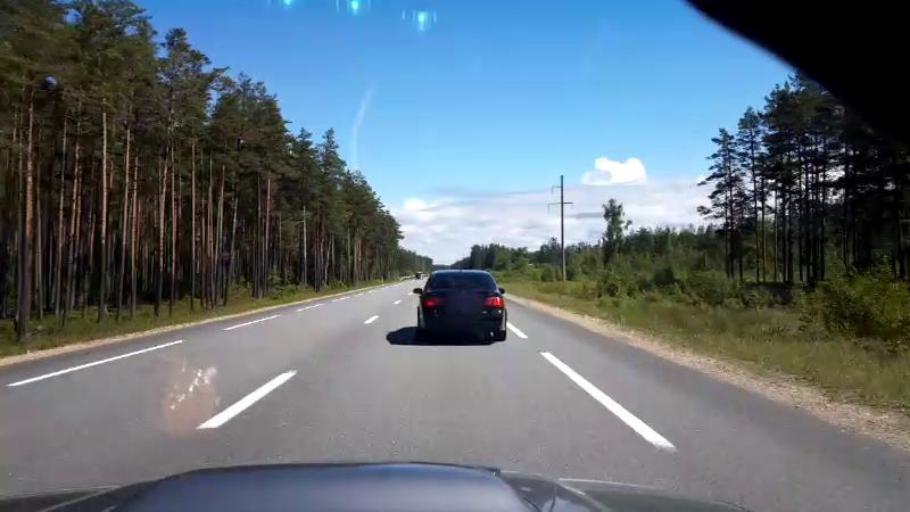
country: LV
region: Saulkrastu
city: Saulkrasti
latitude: 57.2193
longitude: 24.4059
